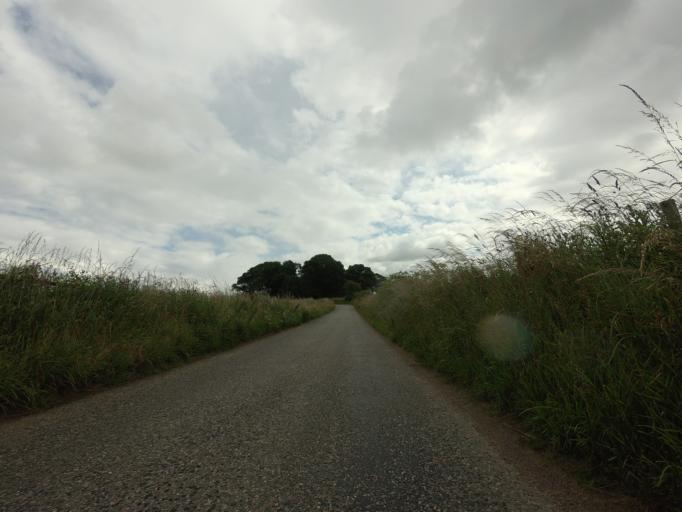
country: GB
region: Scotland
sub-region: Moray
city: Lhanbryd
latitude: 57.6476
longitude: -3.2441
